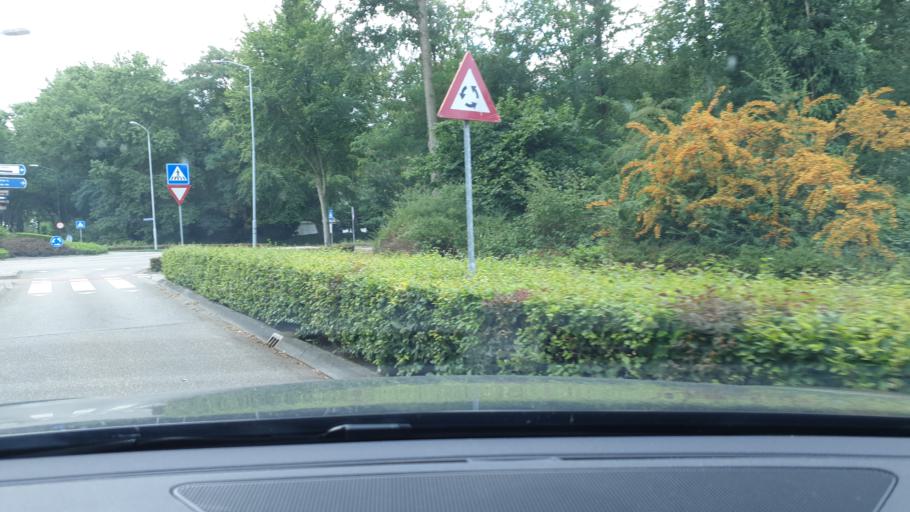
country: NL
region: North Brabant
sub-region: Gemeente Veldhoven
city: Oerle
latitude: 51.4192
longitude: 5.3783
